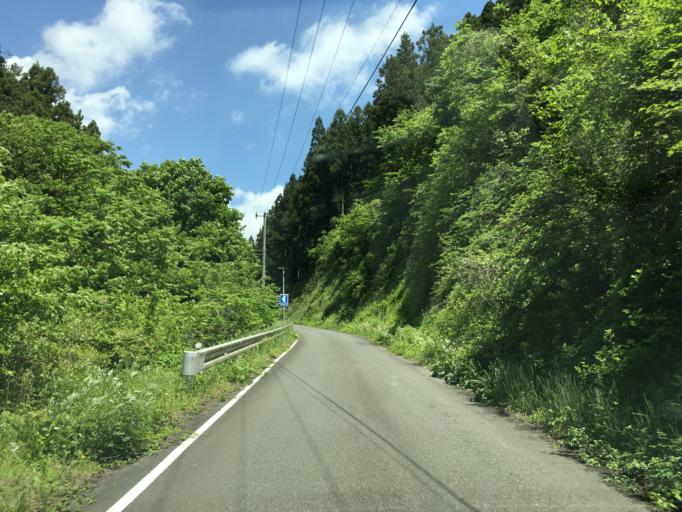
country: JP
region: Miyagi
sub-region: Oshika Gun
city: Onagawa Cho
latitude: 38.6766
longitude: 141.3476
